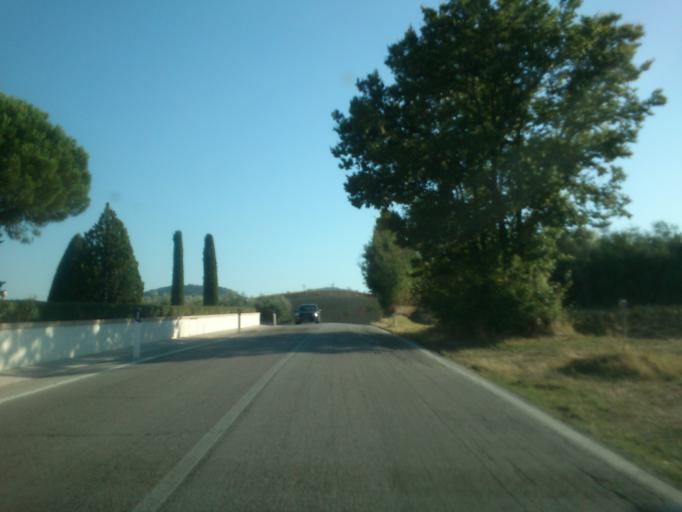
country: IT
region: The Marches
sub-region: Provincia di Pesaro e Urbino
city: Mombaroccio
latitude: 43.8156
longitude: 12.8632
